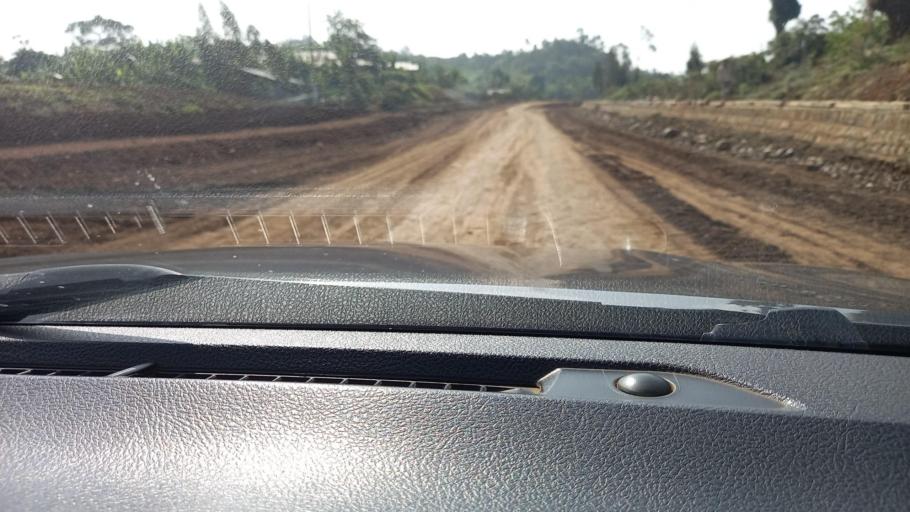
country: ET
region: Southern Nations, Nationalities, and People's Region
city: Mizan Teferi
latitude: 6.1651
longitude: 35.5915
